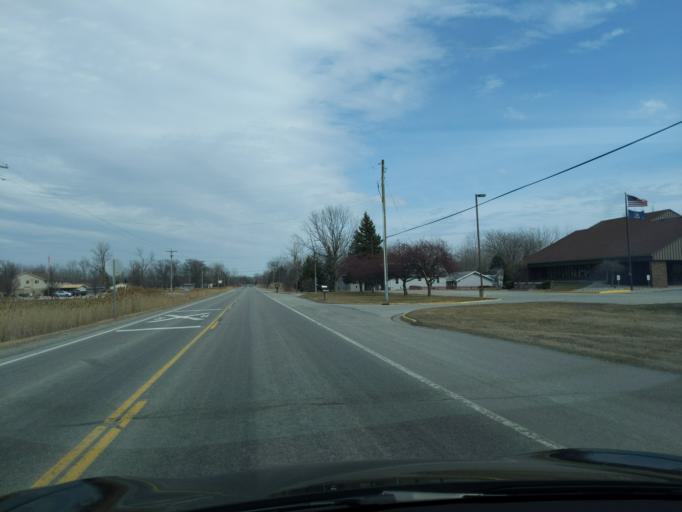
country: US
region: Michigan
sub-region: Bay County
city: Bay City
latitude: 43.6676
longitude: -83.9467
